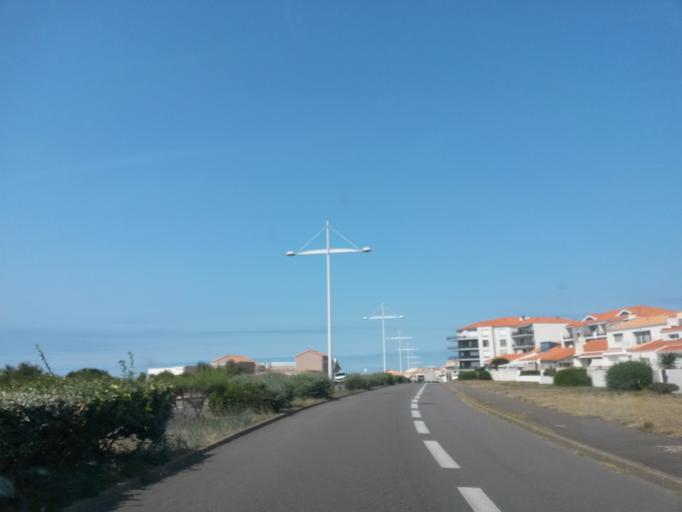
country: FR
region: Pays de la Loire
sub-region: Departement de la Vendee
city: Les Sables-d'Olonne
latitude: 46.4904
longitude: -1.8034
